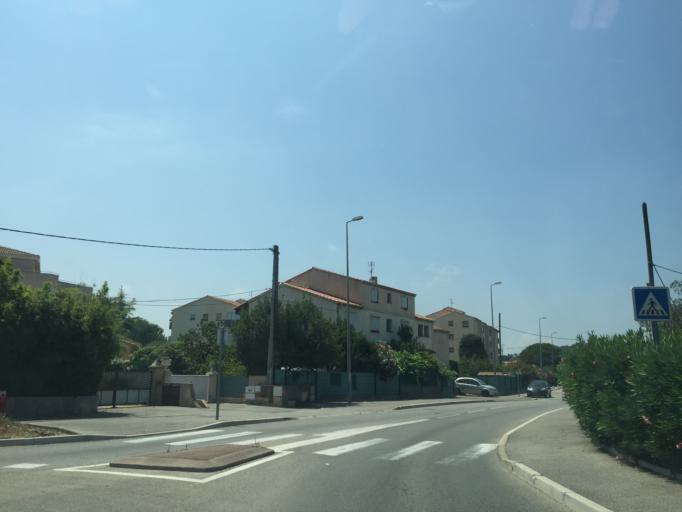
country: FR
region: Provence-Alpes-Cote d'Azur
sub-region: Departement du Var
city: Frejus
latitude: 43.4346
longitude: 6.7496
